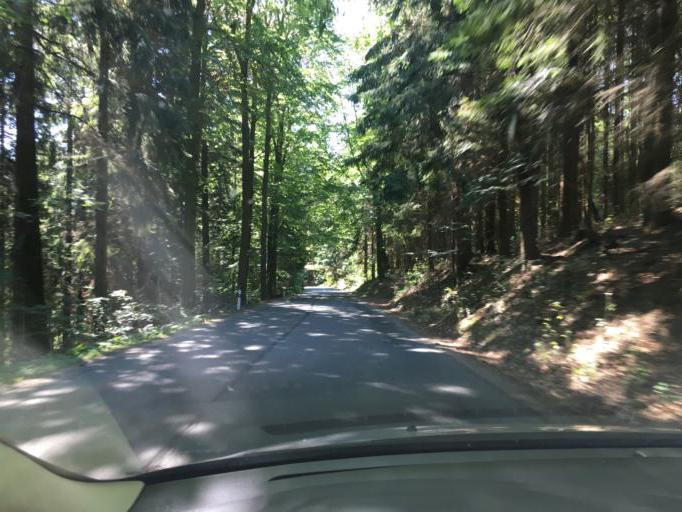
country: CZ
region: Liberecky
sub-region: Okres Semily
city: Vysoke nad Jizerou
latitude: 50.7063
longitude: 15.3722
